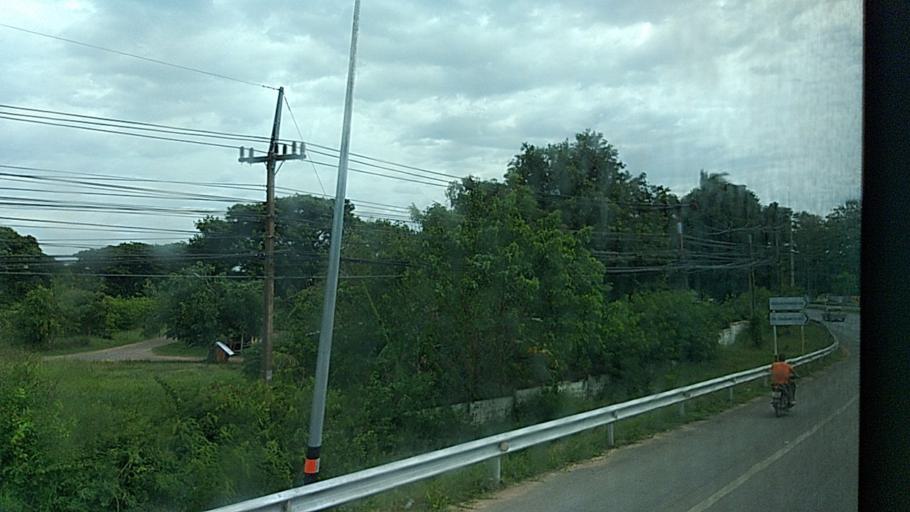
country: TH
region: Maha Sarakham
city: Maha Sarakham
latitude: 16.2043
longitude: 103.2874
